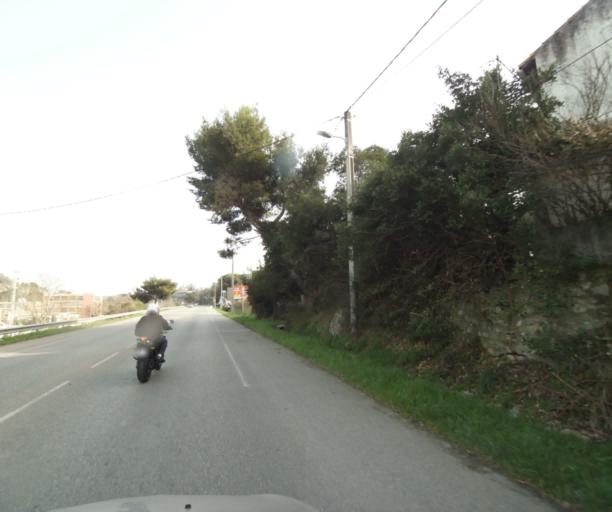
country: FR
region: Provence-Alpes-Cote d'Azur
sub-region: Departement des Bouches-du-Rhone
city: Les Pennes-Mirabeau
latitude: 43.4137
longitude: 5.3001
